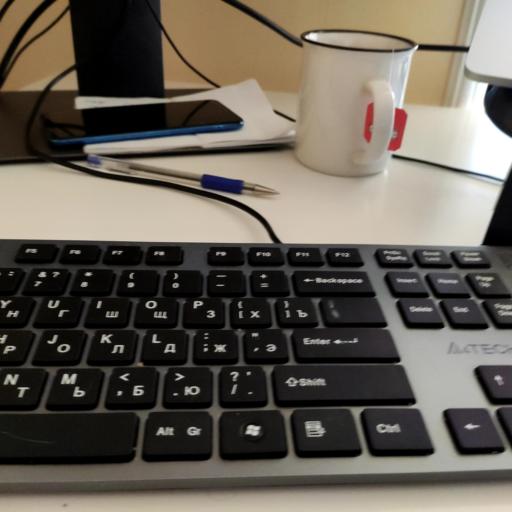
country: RU
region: Moskovskaya
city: Shaburnovo
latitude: 56.5666
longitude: 37.9593
